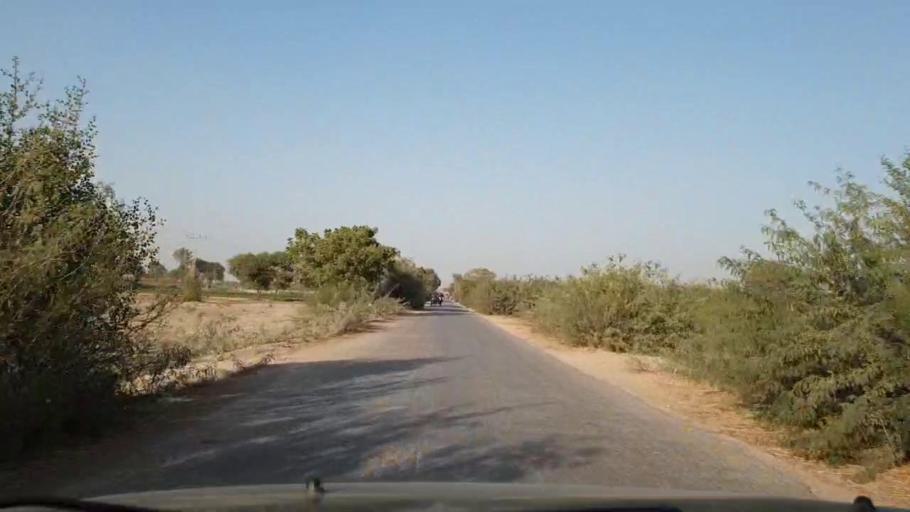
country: PK
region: Sindh
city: Chambar
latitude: 25.2388
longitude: 68.7858
